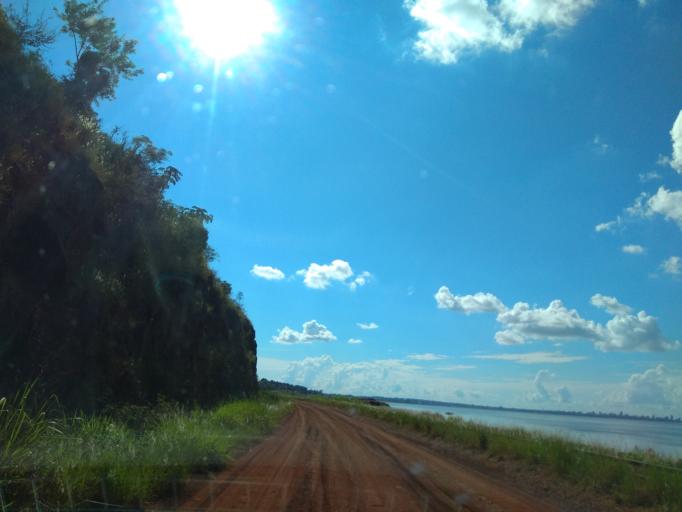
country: AR
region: Misiones
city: Garupa
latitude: -27.4457
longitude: -55.8425
